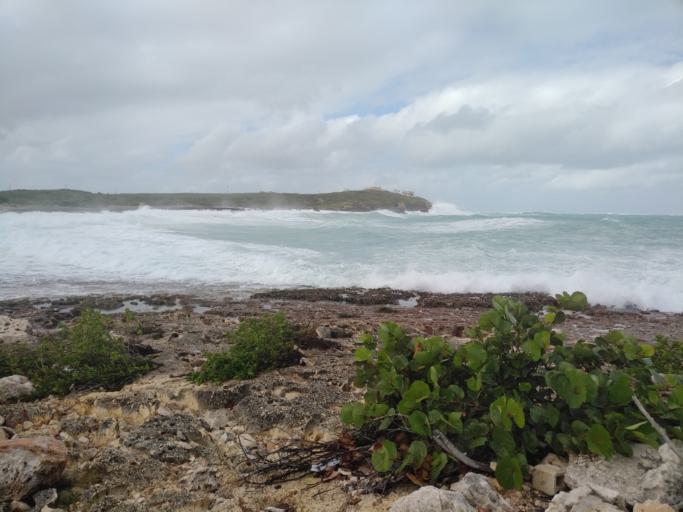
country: AI
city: Island Harbour
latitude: 18.2644
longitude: -62.9797
